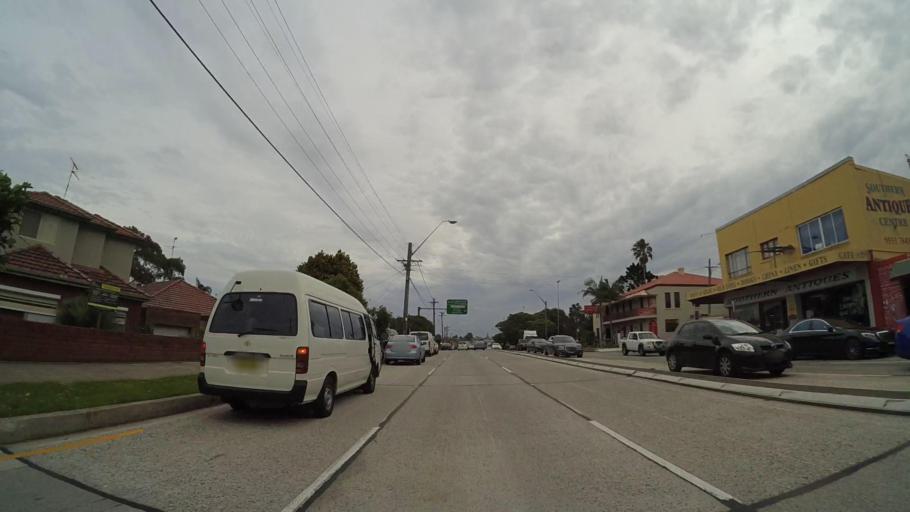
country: AU
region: New South Wales
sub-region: Kogarah
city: Beverly Park
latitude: -33.9723
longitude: 151.1315
